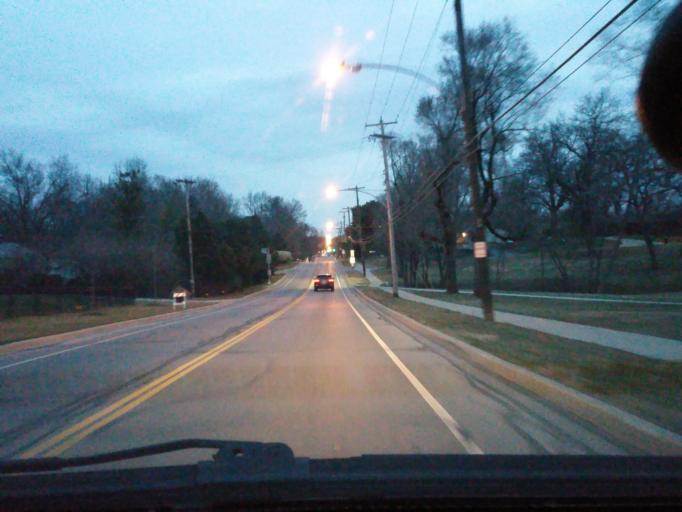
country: US
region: Kansas
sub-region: Johnson County
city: Fairway
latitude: 39.0136
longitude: -94.6304
